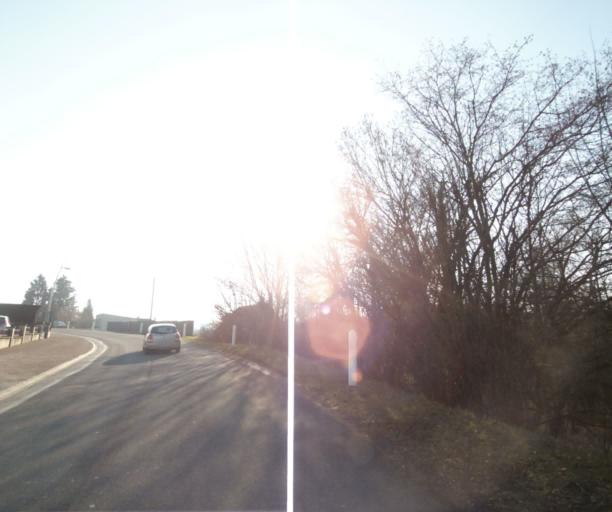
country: FR
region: Champagne-Ardenne
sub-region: Departement de la Haute-Marne
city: Chevillon
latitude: 48.5223
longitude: 5.1167
